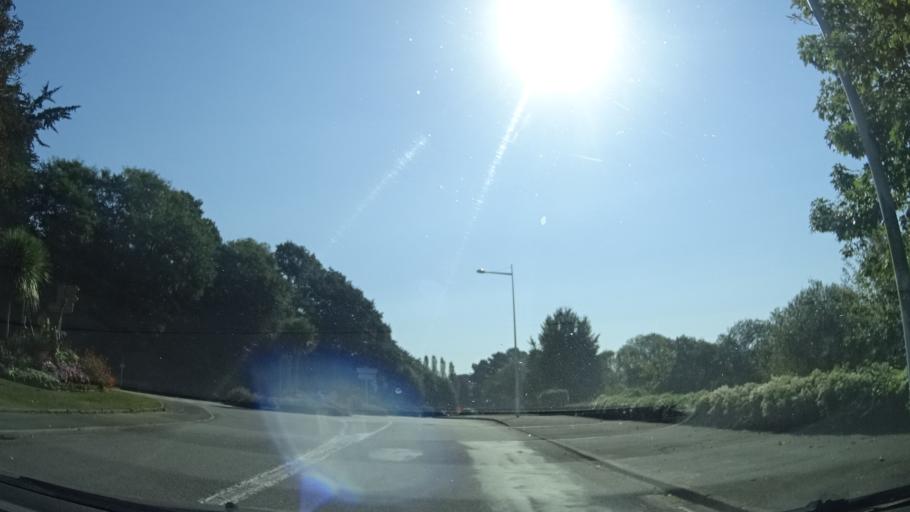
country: FR
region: Brittany
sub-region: Departement du Finistere
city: Douarnenez
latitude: 48.0825
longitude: -4.3297
